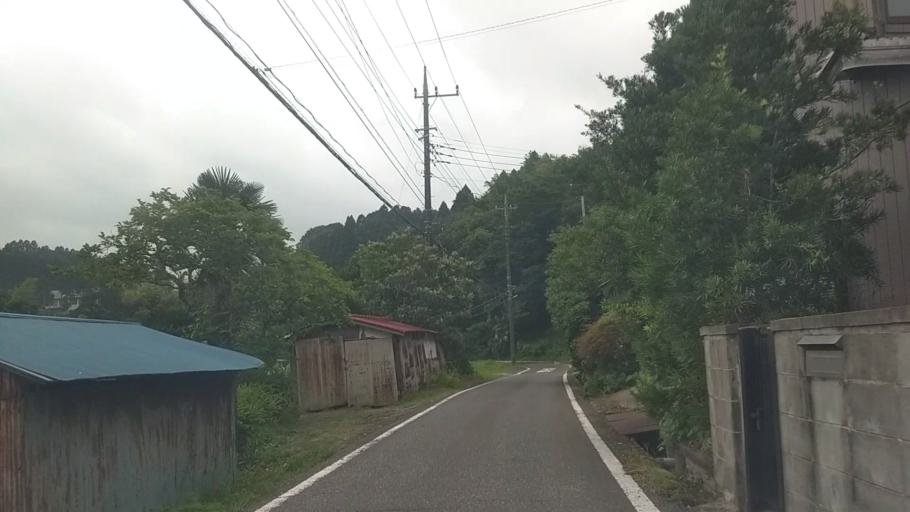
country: JP
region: Chiba
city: Kawaguchi
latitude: 35.2557
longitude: 140.0577
